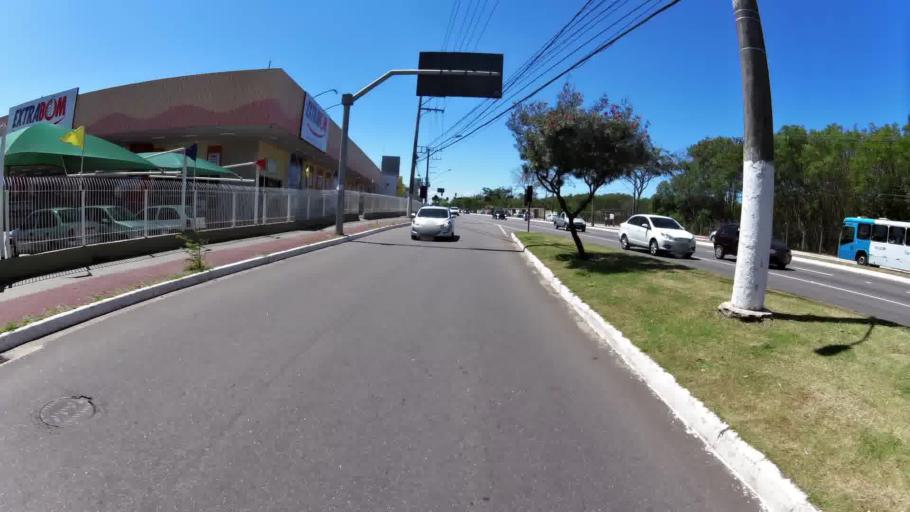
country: BR
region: Espirito Santo
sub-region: Vila Velha
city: Vila Velha
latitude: -20.2642
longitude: -40.2961
